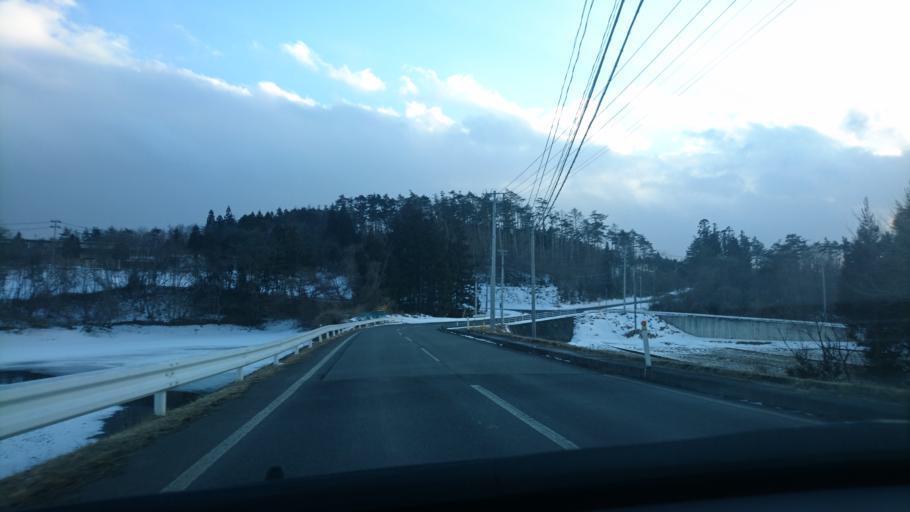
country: JP
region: Iwate
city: Ichinoseki
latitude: 39.0097
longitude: 141.3366
